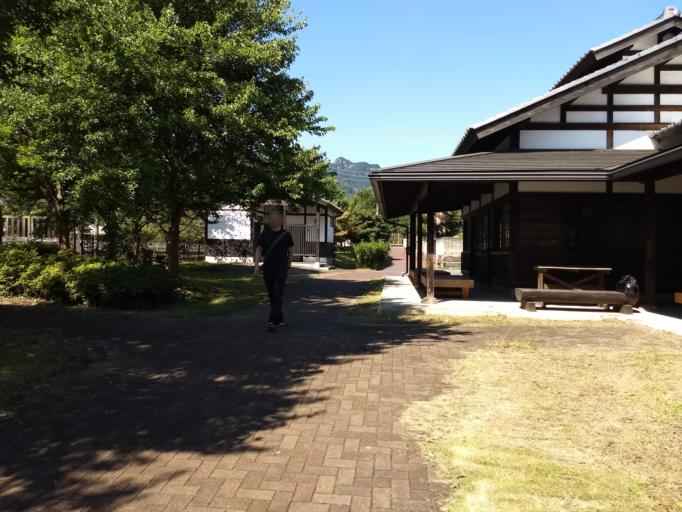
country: JP
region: Gunma
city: Annaka
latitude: 36.3368
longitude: 138.7344
